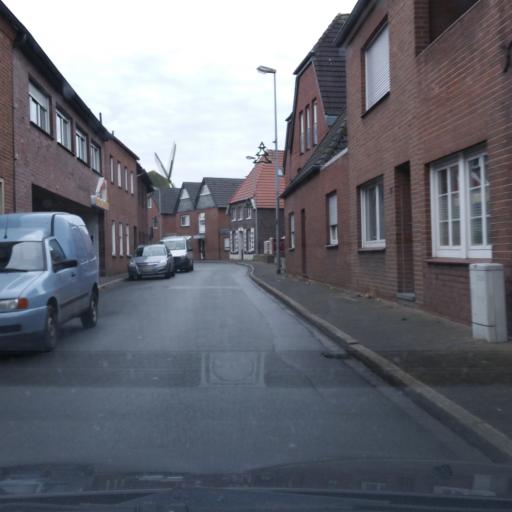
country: DE
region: North Rhine-Westphalia
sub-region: Regierungsbezirk Munster
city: Isselburg
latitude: 51.8201
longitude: 6.5098
